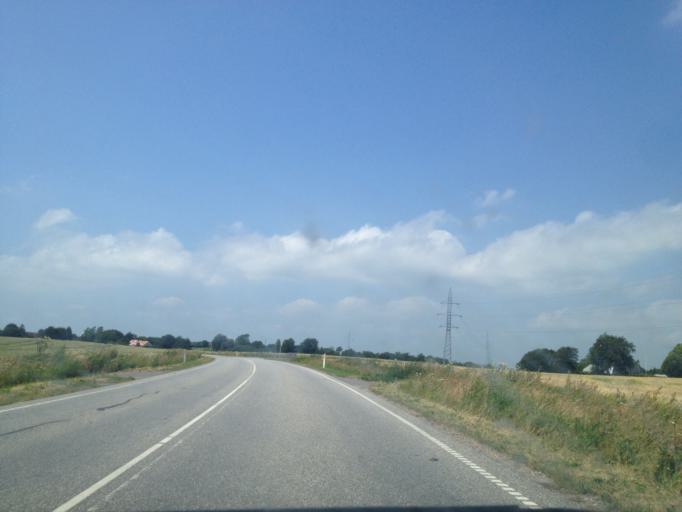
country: DK
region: South Denmark
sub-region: Haderslev Kommune
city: Vojens
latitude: 55.3342
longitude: 9.2998
